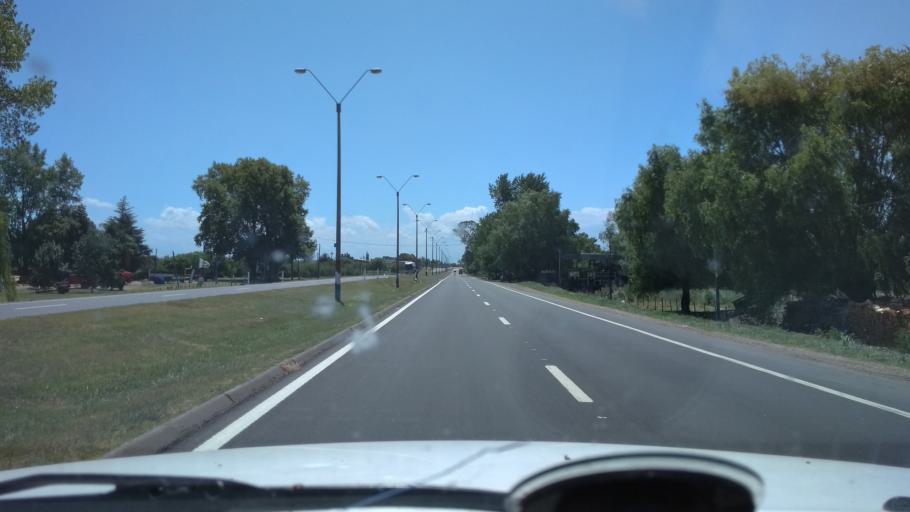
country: UY
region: Canelones
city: Canelones
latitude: -34.5519
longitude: -56.2714
